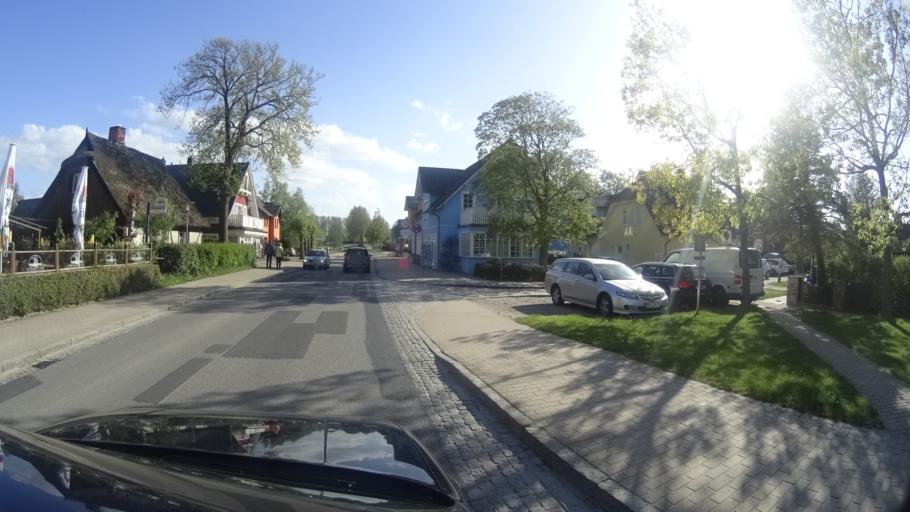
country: DE
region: Mecklenburg-Vorpommern
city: Ostseebad Dierhagen
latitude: 54.3796
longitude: 12.4186
